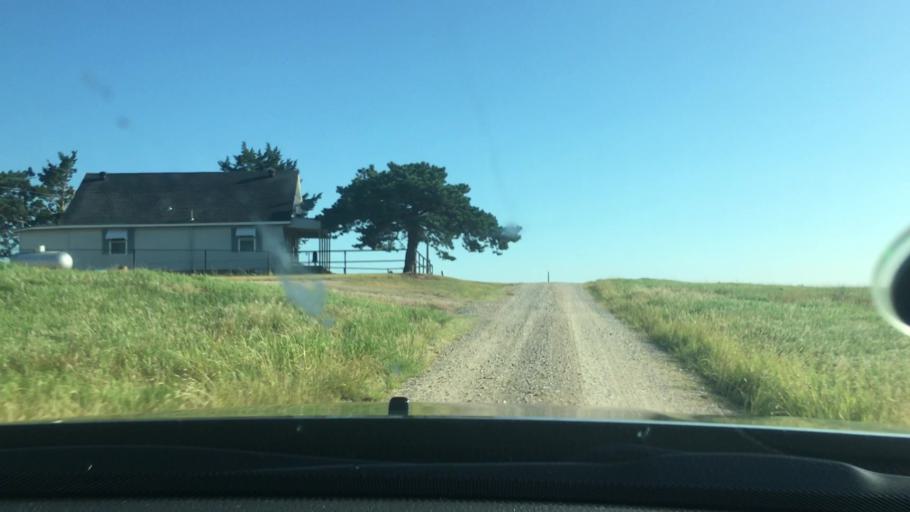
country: US
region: Oklahoma
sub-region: Johnston County
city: Tishomingo
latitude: 34.4143
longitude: -96.7630
